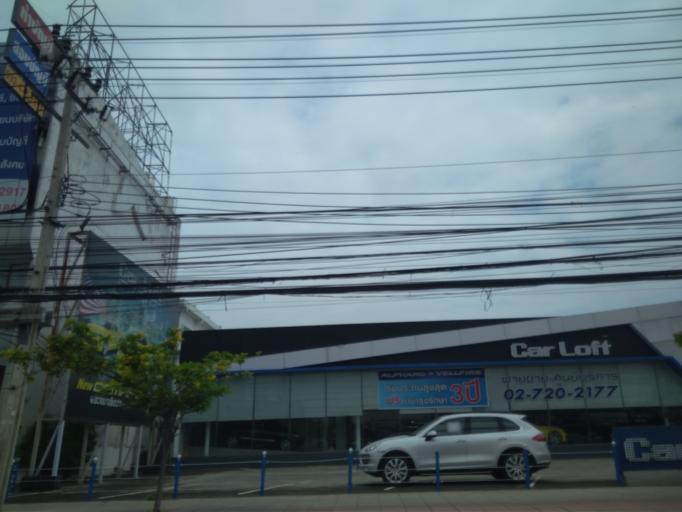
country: TH
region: Bangkok
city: Suan Luang
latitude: 13.6998
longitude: 100.6470
